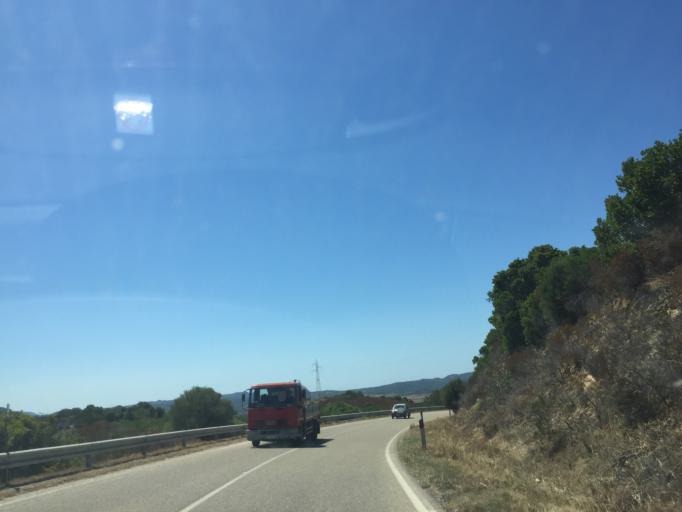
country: IT
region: Sardinia
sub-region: Provincia di Olbia-Tempio
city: Aglientu
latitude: 41.0982
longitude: 9.0893
